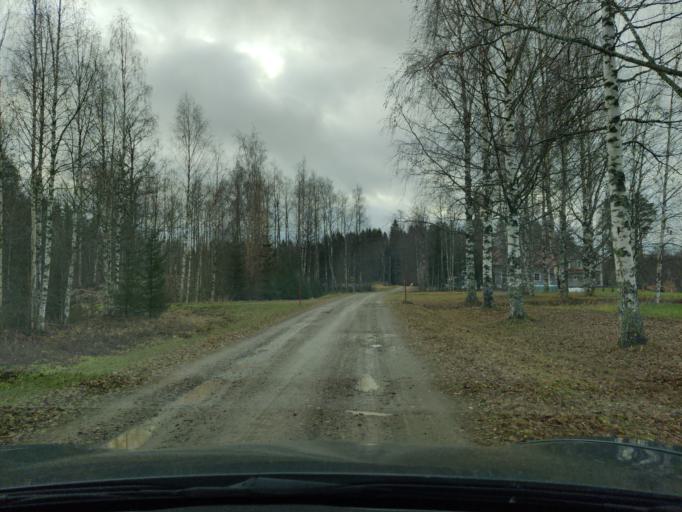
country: FI
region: Northern Savo
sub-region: Ylae-Savo
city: Kiuruvesi
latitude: 63.6410
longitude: 26.6546
